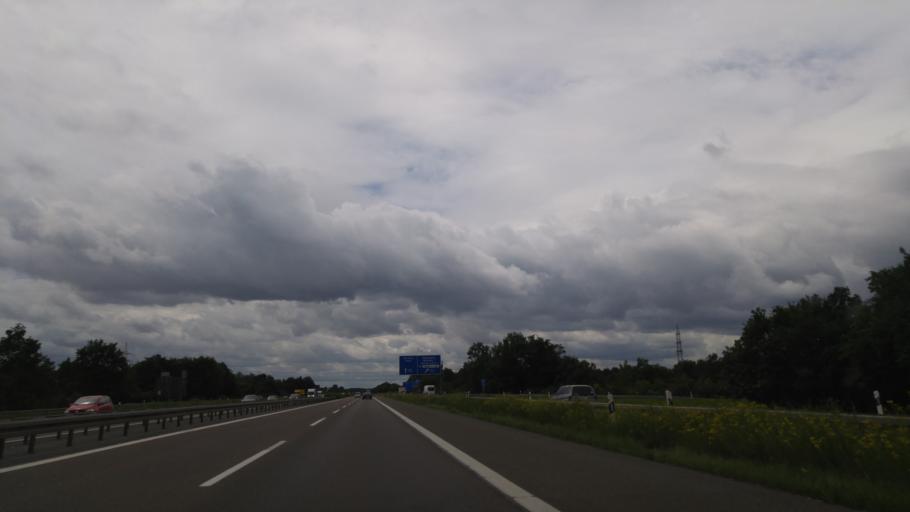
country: DE
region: Bavaria
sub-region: Regierungsbezirk Mittelfranken
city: Erlangen
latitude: 49.5620
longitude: 10.9916
